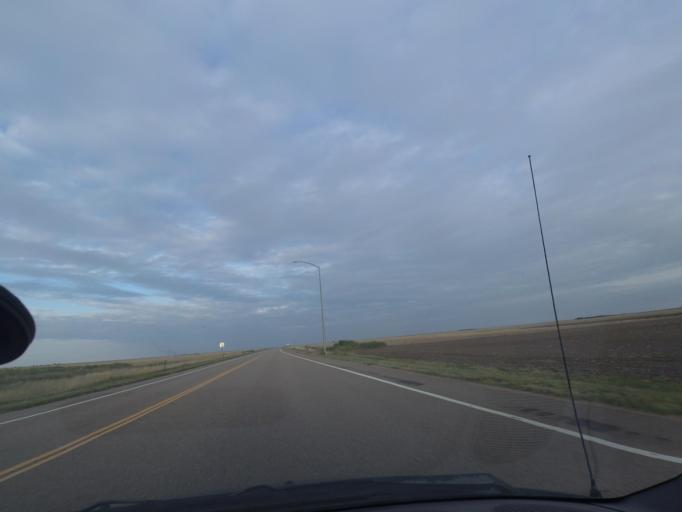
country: US
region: Colorado
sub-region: Yuma County
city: Wray
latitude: 39.7461
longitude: -102.2475
